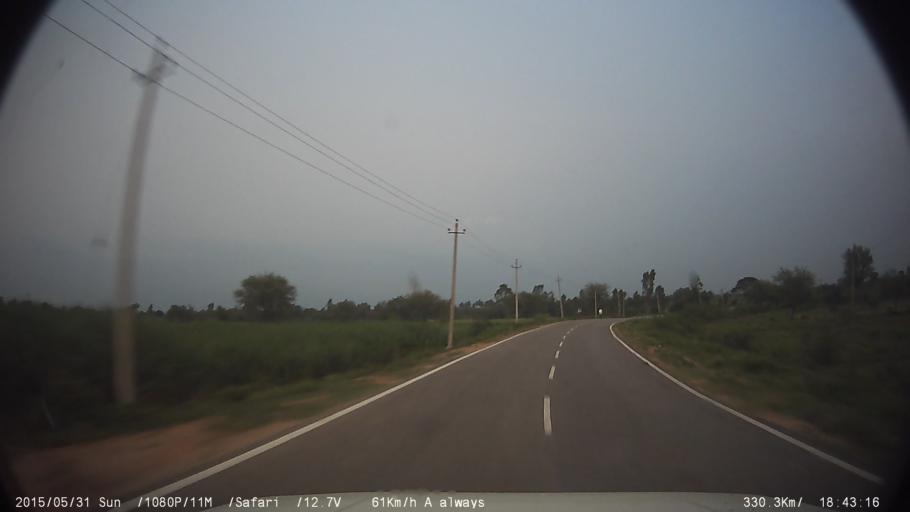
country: IN
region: Karnataka
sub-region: Mysore
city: Tirumakudal Narsipur
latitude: 12.1557
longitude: 76.8053
